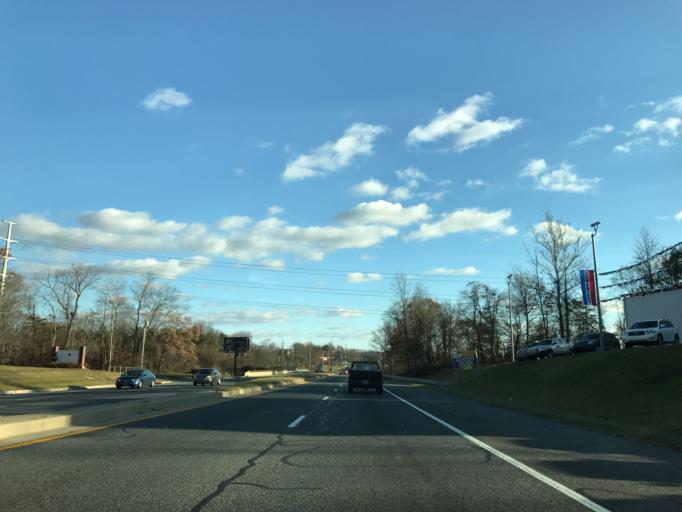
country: US
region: Maryland
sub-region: Harford County
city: Joppatowne
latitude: 39.4355
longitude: -76.3415
